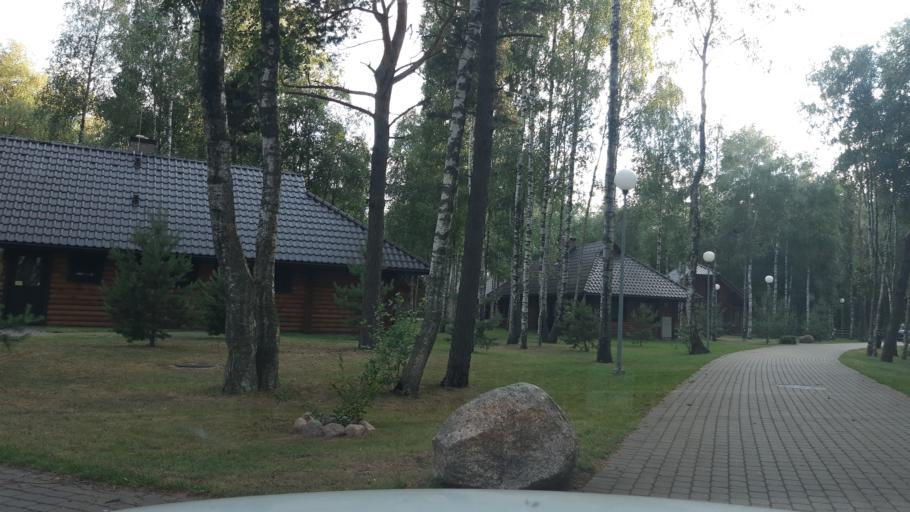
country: LT
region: Klaipedos apskritis
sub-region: Klaipeda
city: Palanga
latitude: 55.9593
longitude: 21.1240
